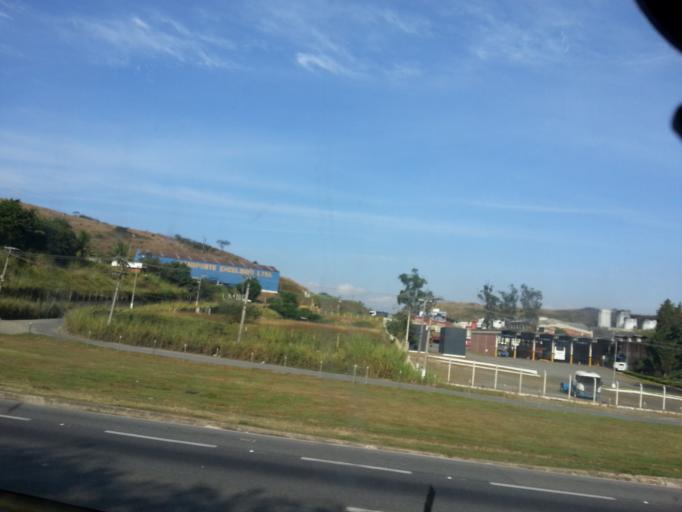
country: BR
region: Rio de Janeiro
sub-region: Volta Redonda
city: Volta Redonda
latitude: -22.5584
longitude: -44.1250
